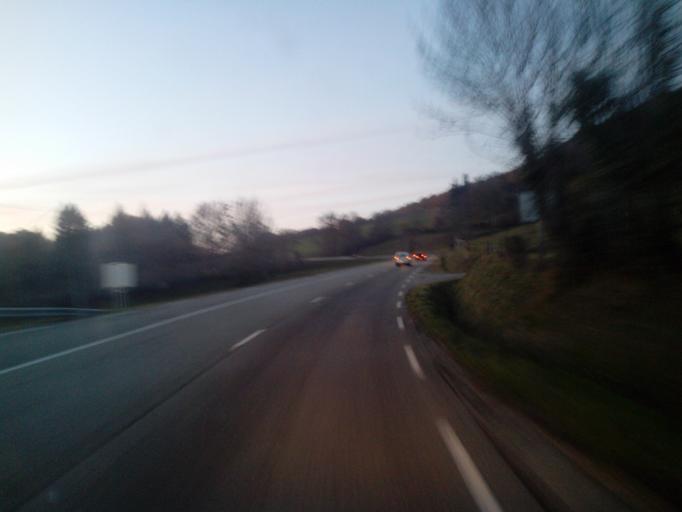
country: FR
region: Midi-Pyrenees
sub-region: Departement de l'Ariege
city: Foix
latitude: 42.9702
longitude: 1.5861
